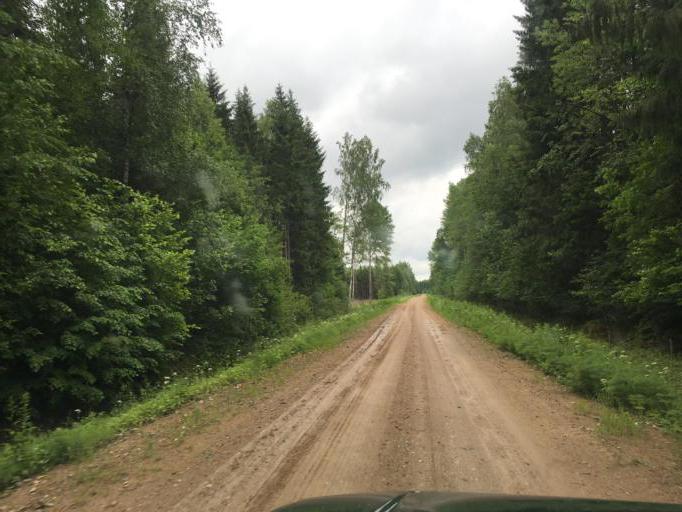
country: LV
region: Vilaka
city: Vilaka
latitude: 57.3747
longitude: 27.4727
